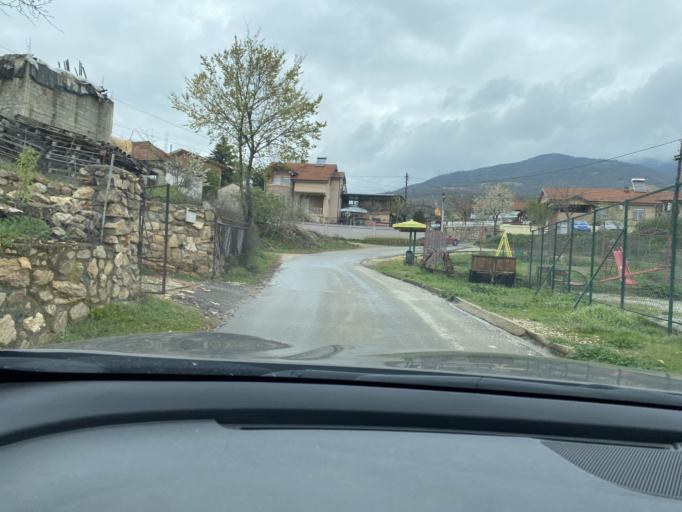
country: MK
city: Creshevo
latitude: 42.0513
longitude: 21.5187
